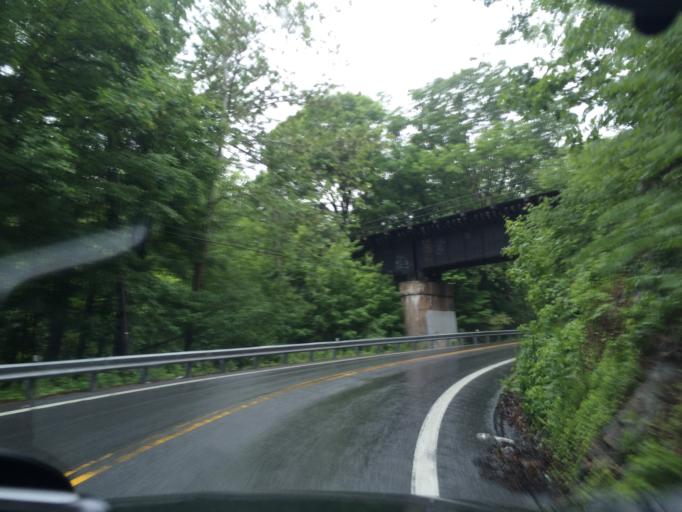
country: US
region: Maryland
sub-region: Frederick County
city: Thurmont
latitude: 39.6491
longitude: -77.4267
